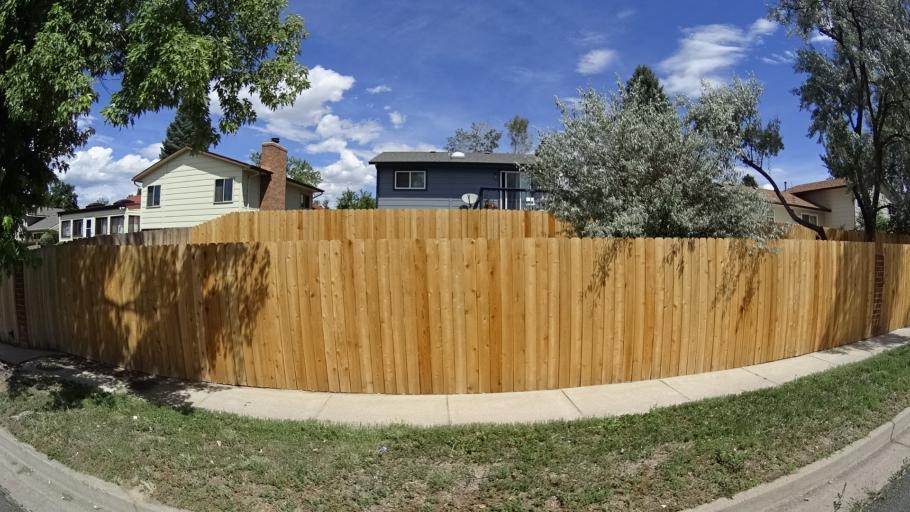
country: US
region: Colorado
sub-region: El Paso County
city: Black Forest
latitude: 38.9431
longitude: -104.7596
